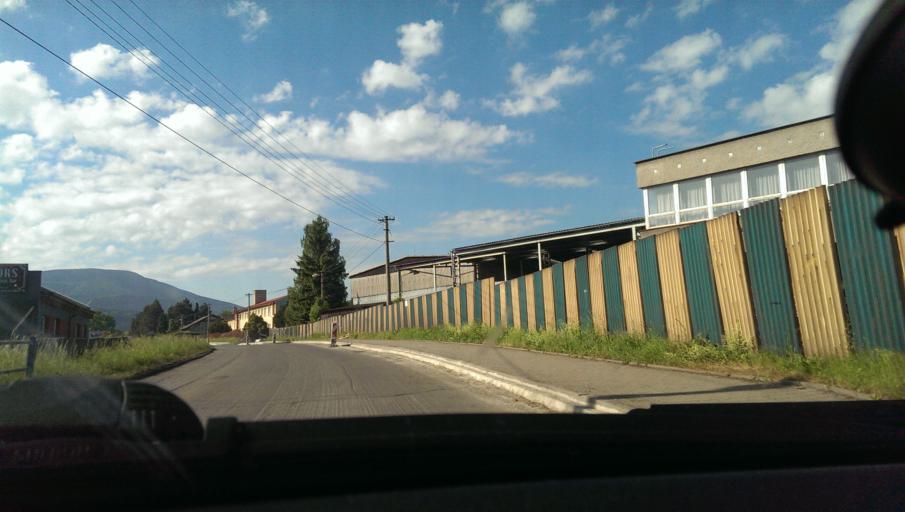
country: CZ
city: Frydlant nad Ostravici
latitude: 49.5819
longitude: 18.3582
